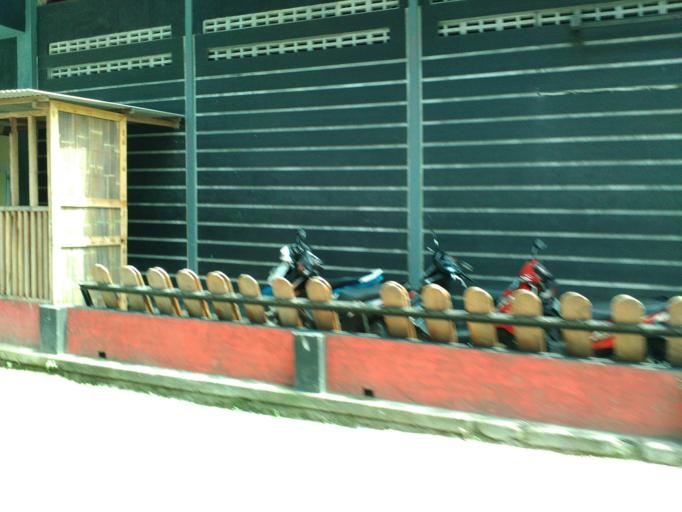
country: ID
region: Central Java
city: Klaten
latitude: -7.7053
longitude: 110.5977
